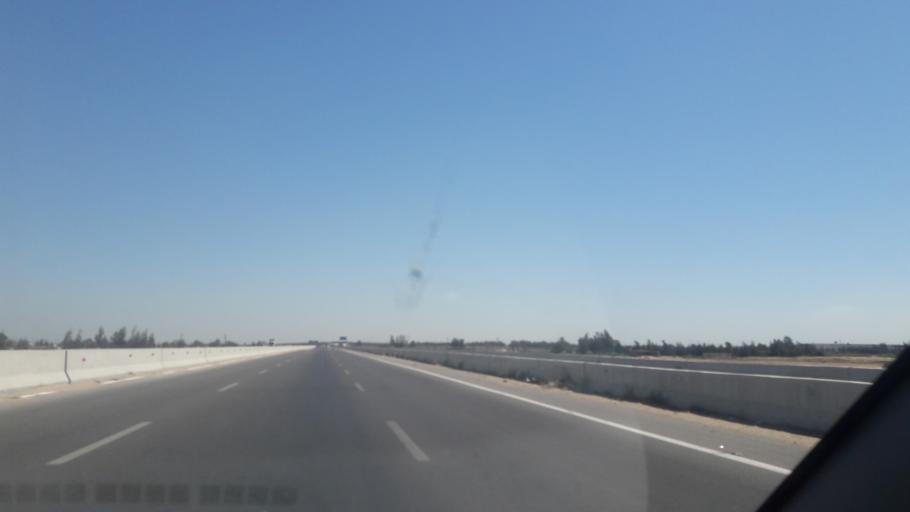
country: EG
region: Al Isma'iliyah
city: Ismailia
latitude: 30.8190
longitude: 32.1662
